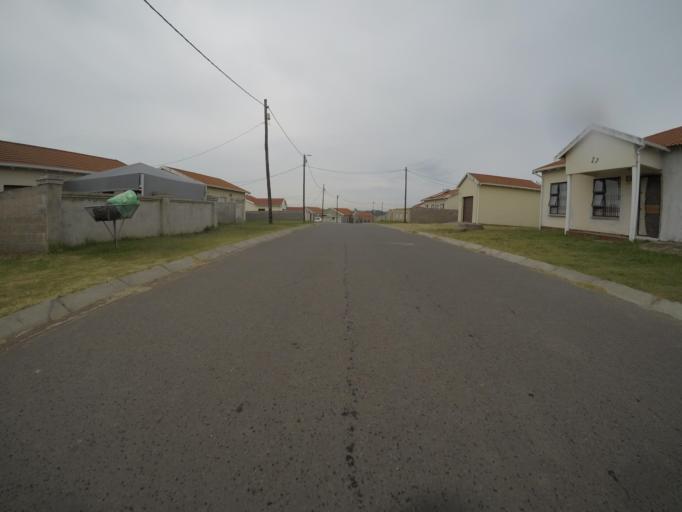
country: ZA
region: Eastern Cape
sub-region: Buffalo City Metropolitan Municipality
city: East London
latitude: -33.0033
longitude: 27.8508
